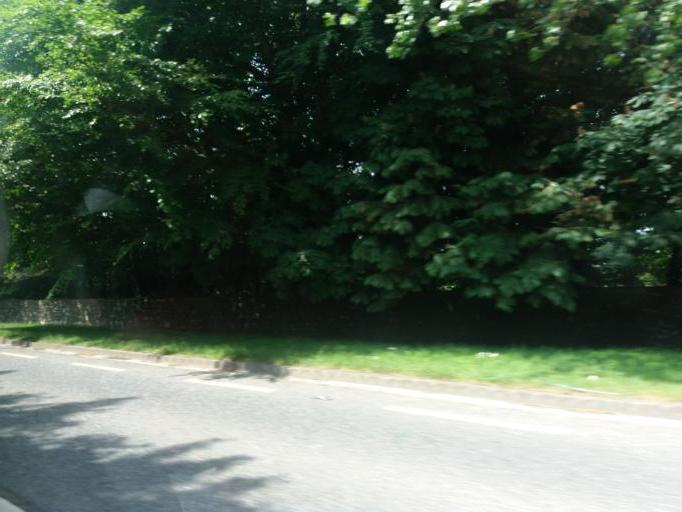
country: IE
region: Leinster
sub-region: An Mhi
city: Slane
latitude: 53.6958
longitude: -6.6050
